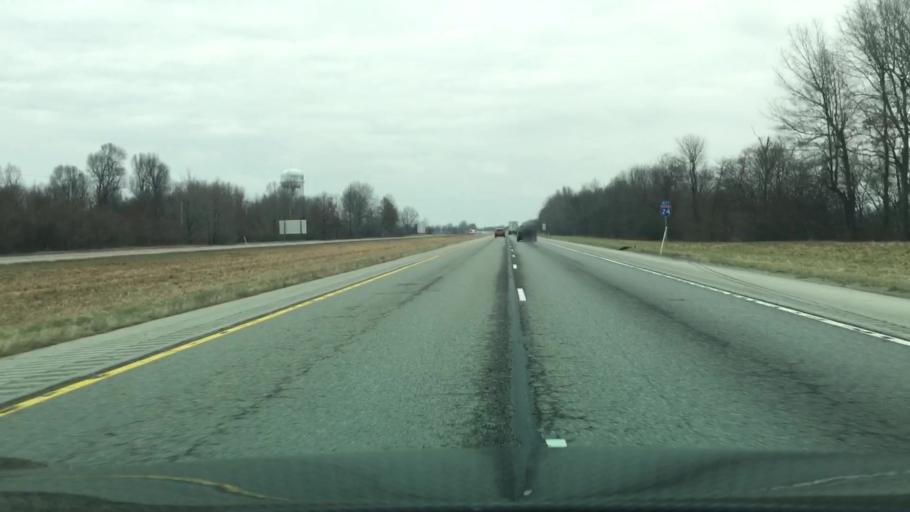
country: US
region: Illinois
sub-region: Massac County
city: Metropolis
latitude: 37.1682
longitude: -88.6824
